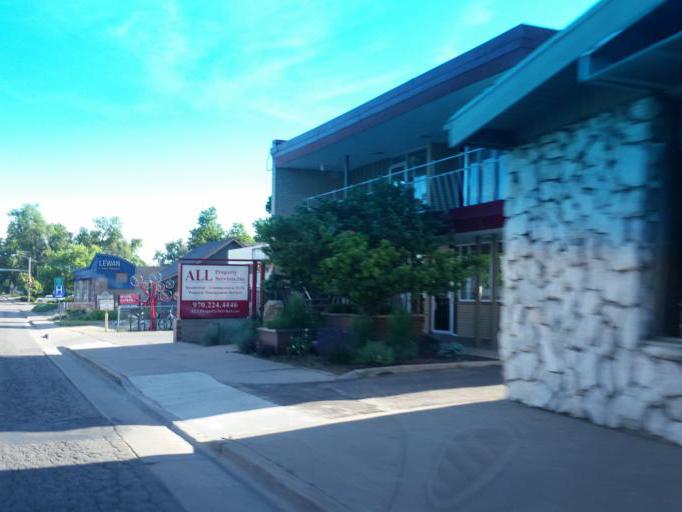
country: US
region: Colorado
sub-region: Larimer County
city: Fort Collins
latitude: 40.5658
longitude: -105.0769
